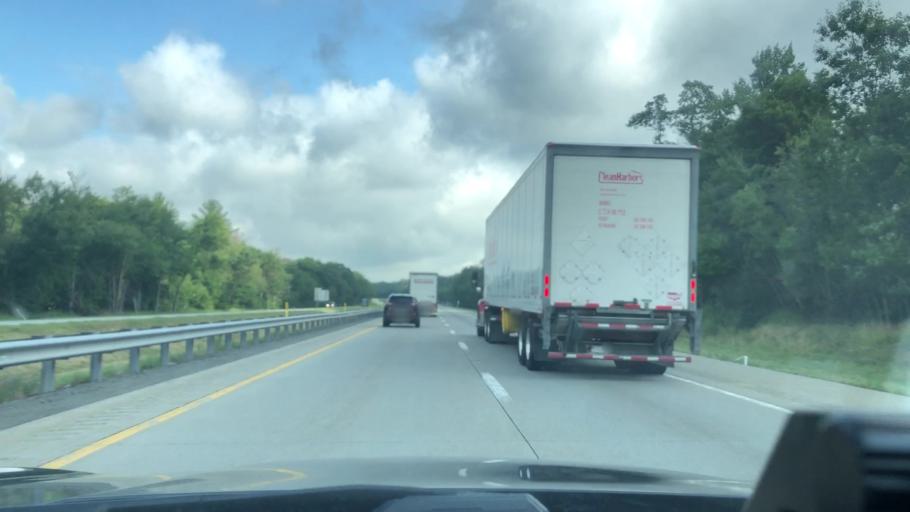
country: US
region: Pennsylvania
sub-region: Monroe County
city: Mount Pocono
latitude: 41.1337
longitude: -75.4009
